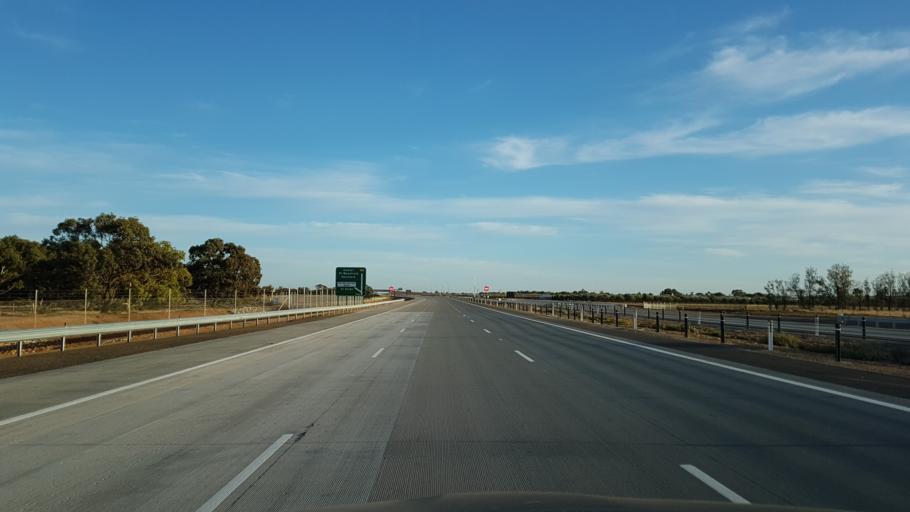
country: AU
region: South Australia
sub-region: Salisbury
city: Salisbury
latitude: -34.7465
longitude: 138.5805
